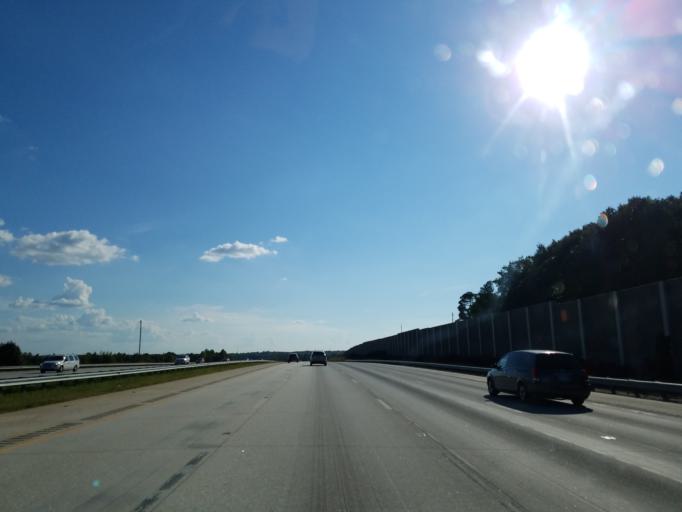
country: US
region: North Carolina
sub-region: Rowan County
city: Spencer
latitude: 35.7287
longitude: -80.3807
